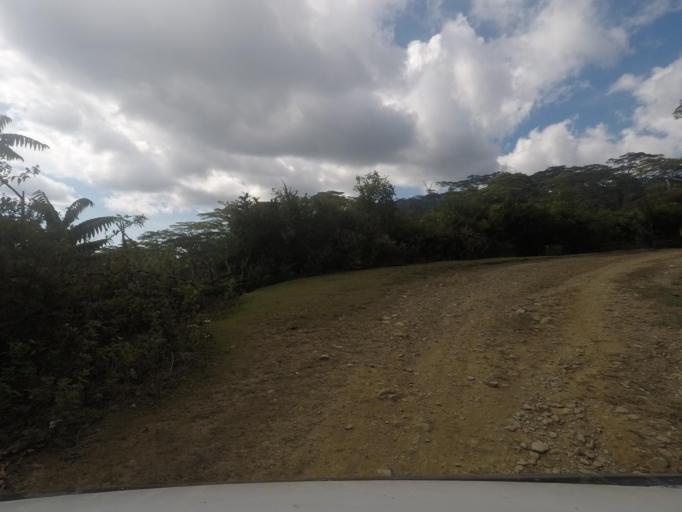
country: TL
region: Ermera
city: Gleno
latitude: -8.7476
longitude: 125.3240
